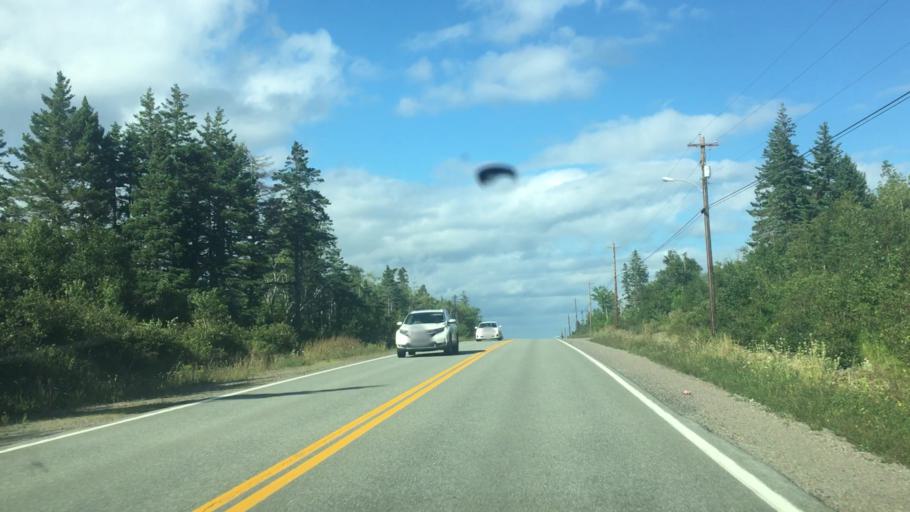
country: CA
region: Nova Scotia
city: Sydney
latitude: 45.8557
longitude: -60.6298
